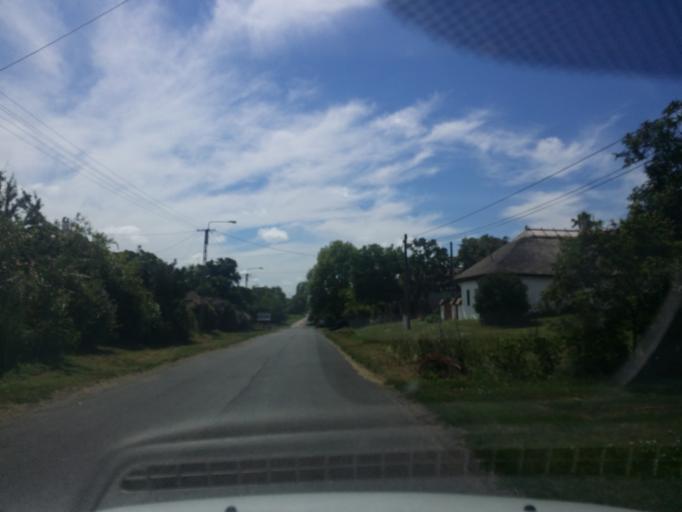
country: HU
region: Heves
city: Tiszanana
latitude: 47.5851
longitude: 20.5993
